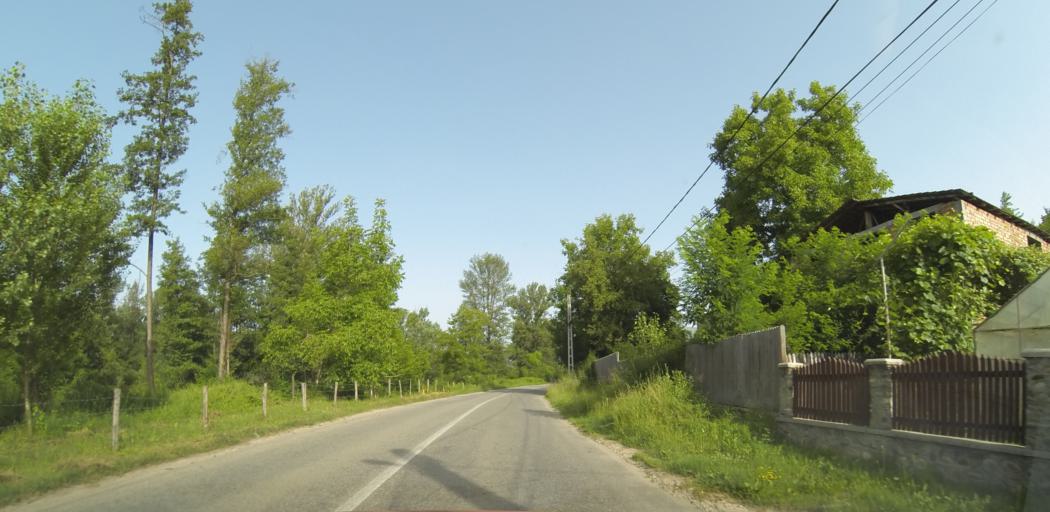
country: RO
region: Valcea
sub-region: Comuna Pausesti-Maglasi
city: Pausesti-Maglasi
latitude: 45.1304
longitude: 24.2621
